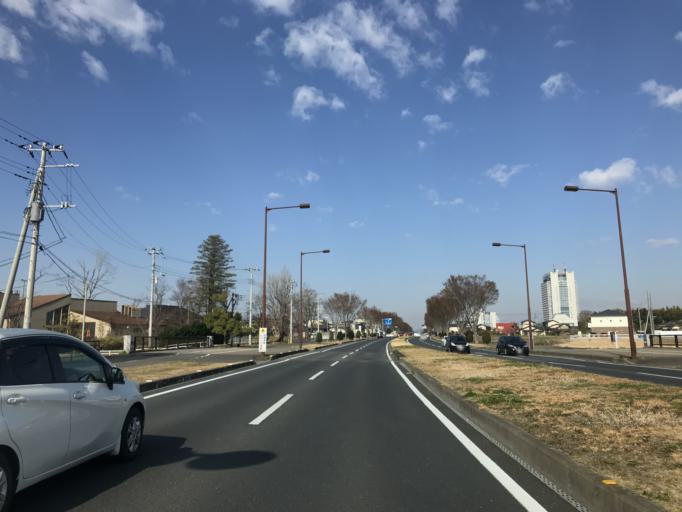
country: JP
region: Ibaraki
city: Mito-shi
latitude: 36.3370
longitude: 140.4581
